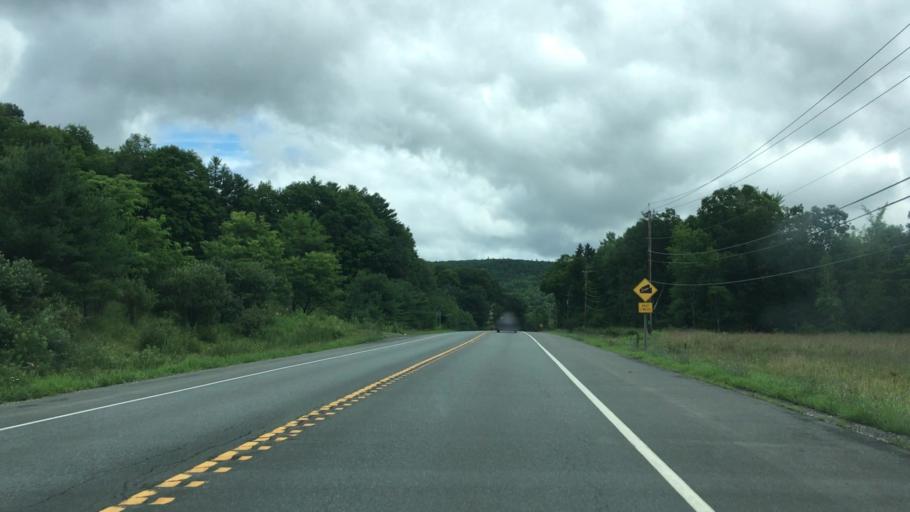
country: US
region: New York
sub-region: Rensselaer County
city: Hoosick Falls
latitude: 42.8449
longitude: -73.3863
